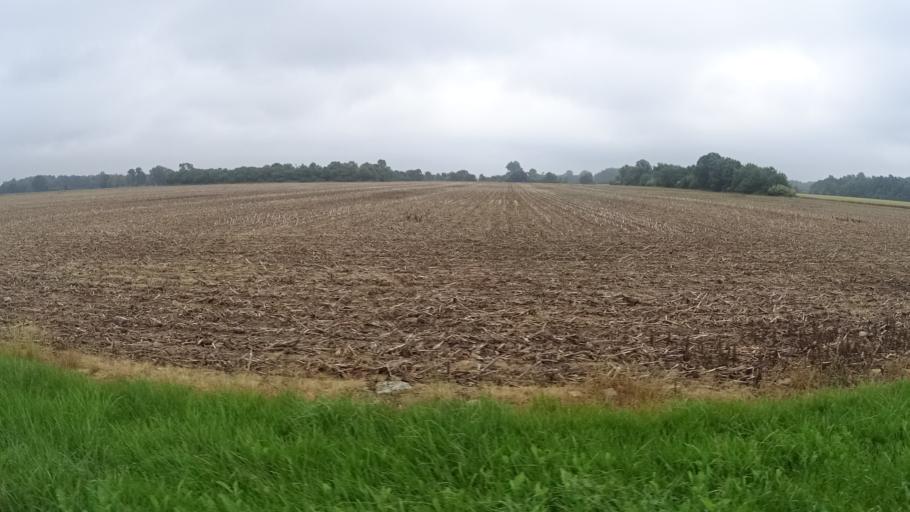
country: US
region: Ohio
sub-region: Huron County
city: Bellevue
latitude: 41.3594
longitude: -82.8172
